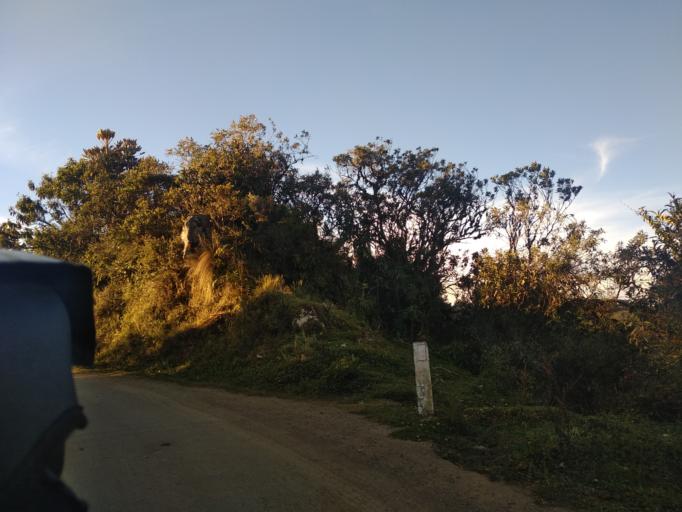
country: PE
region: Amazonas
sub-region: Provincia de Chachapoyas
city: Montevideo
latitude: -6.7105
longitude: -77.8662
